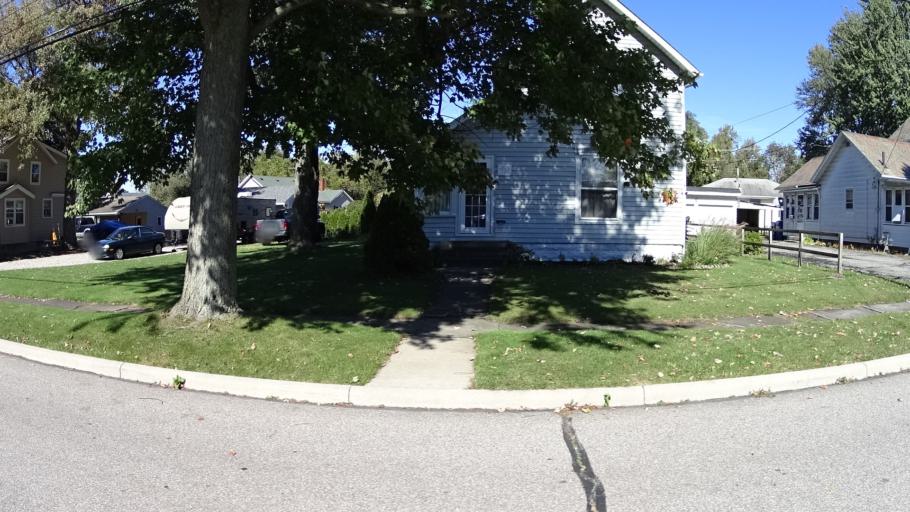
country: US
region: Ohio
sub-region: Lorain County
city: Amherst
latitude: 41.3950
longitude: -82.2216
